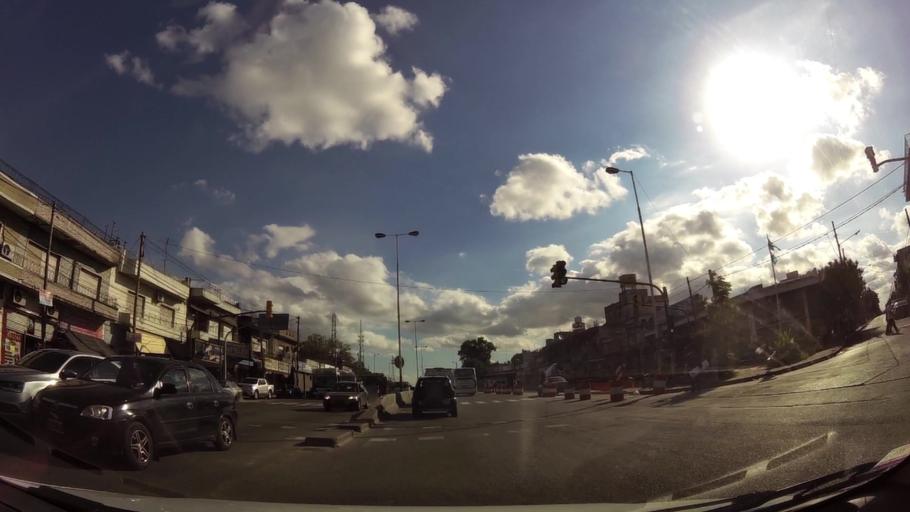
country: AR
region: Buenos Aires
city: San Justo
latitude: -34.7039
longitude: -58.5826
